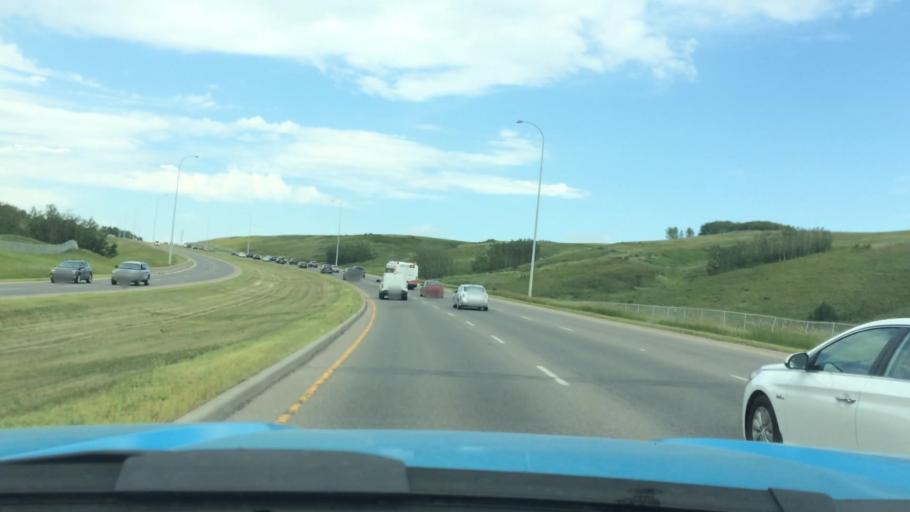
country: CA
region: Alberta
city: Calgary
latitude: 51.1155
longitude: -114.1341
